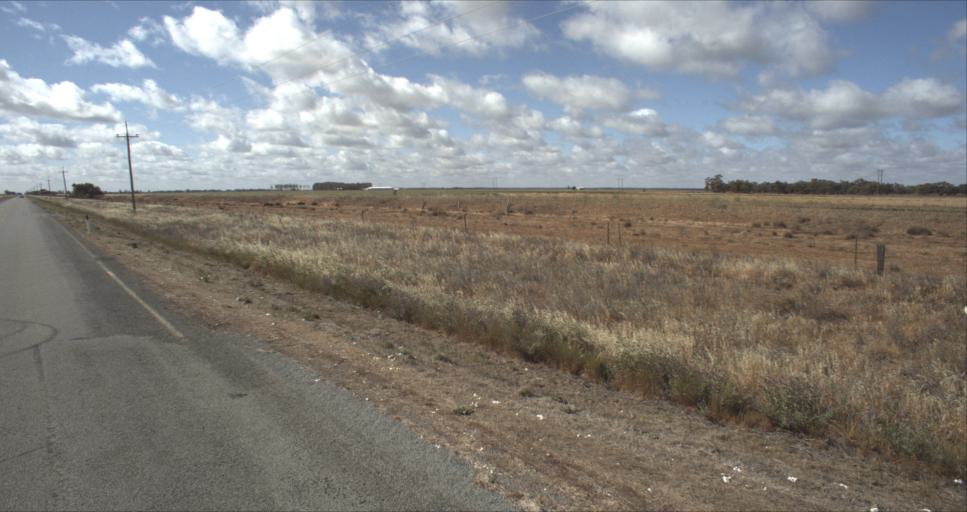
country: AU
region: New South Wales
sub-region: Leeton
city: Leeton
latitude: -34.5231
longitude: 146.2010
